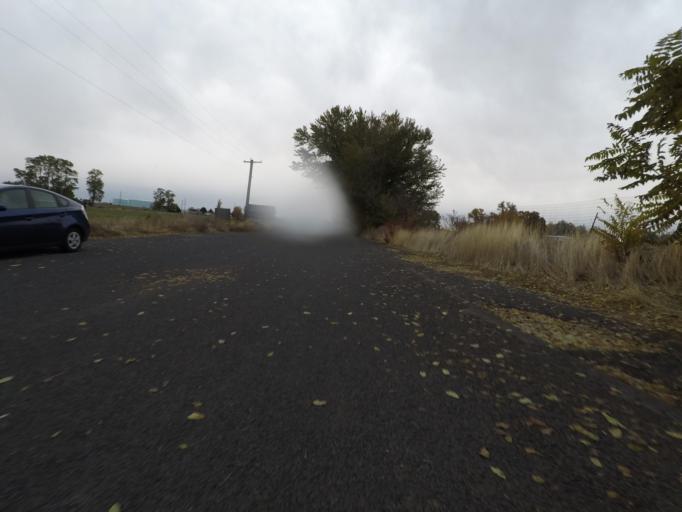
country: US
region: Washington
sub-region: Walla Walla County
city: Walla Walla East
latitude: 46.0828
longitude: -118.2525
